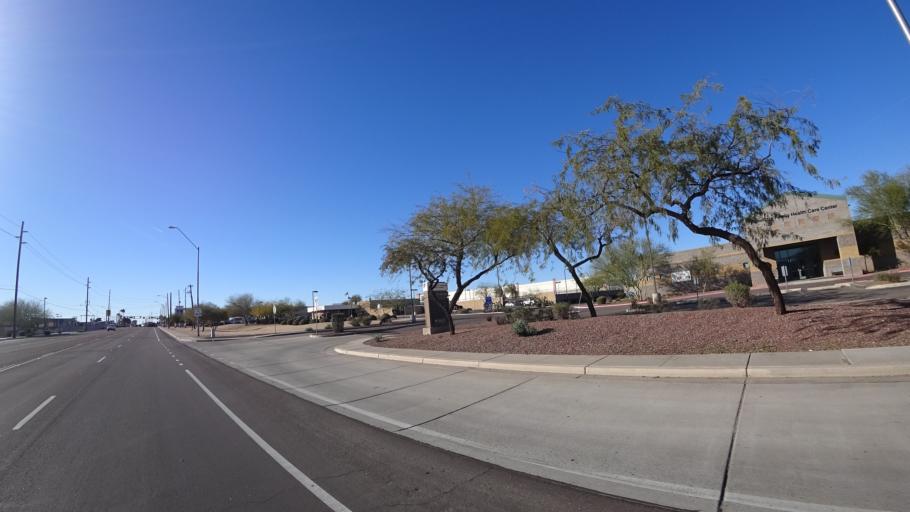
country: US
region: Arizona
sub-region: Maricopa County
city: Avondale
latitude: 33.4498
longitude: -112.3374
